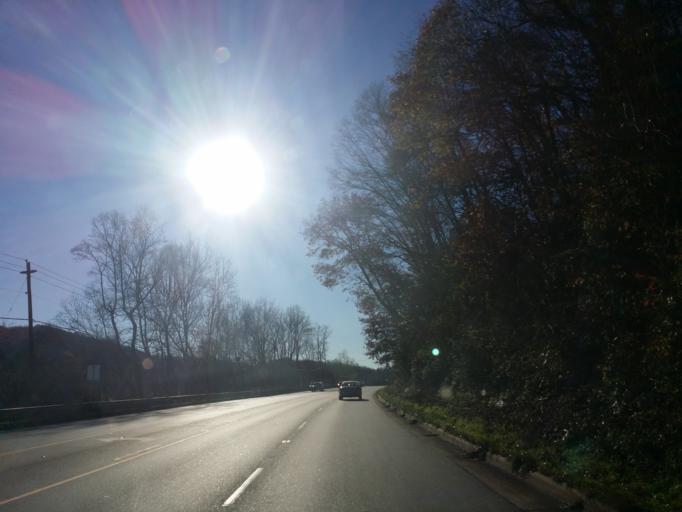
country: US
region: North Carolina
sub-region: Buncombe County
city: Swannanoa
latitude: 35.5858
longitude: -82.4584
